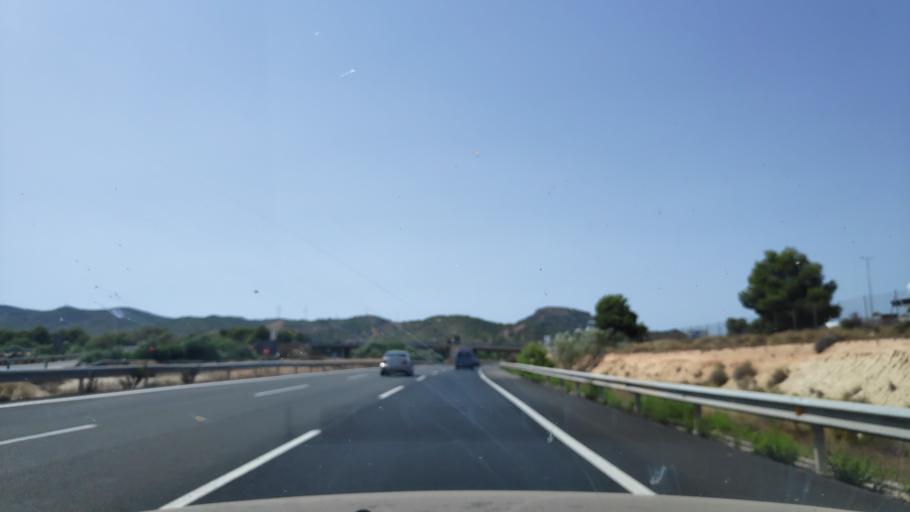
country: ES
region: Murcia
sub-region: Murcia
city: Murcia
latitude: 37.8840
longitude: -1.1365
